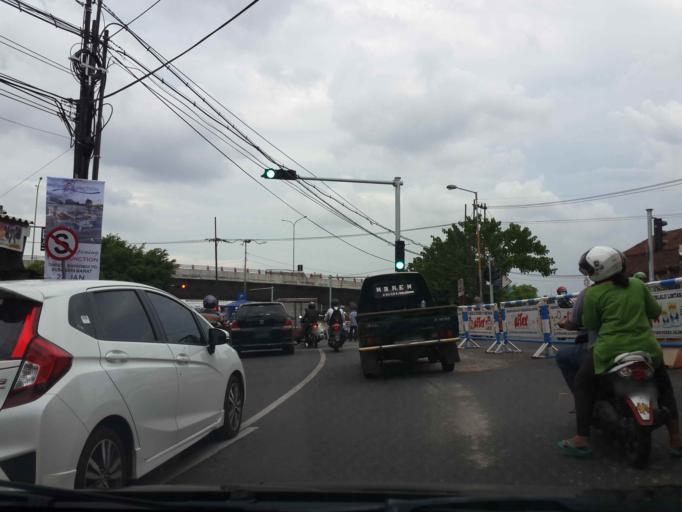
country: ID
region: East Java
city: Gubengairlangga
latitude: -7.2747
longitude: 112.7260
